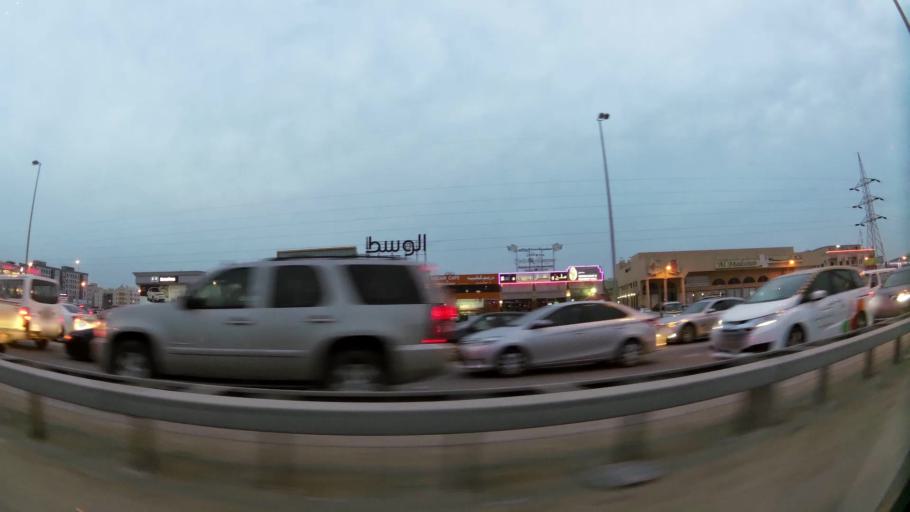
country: BH
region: Northern
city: Ar Rifa'
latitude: 26.1420
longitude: 50.5798
